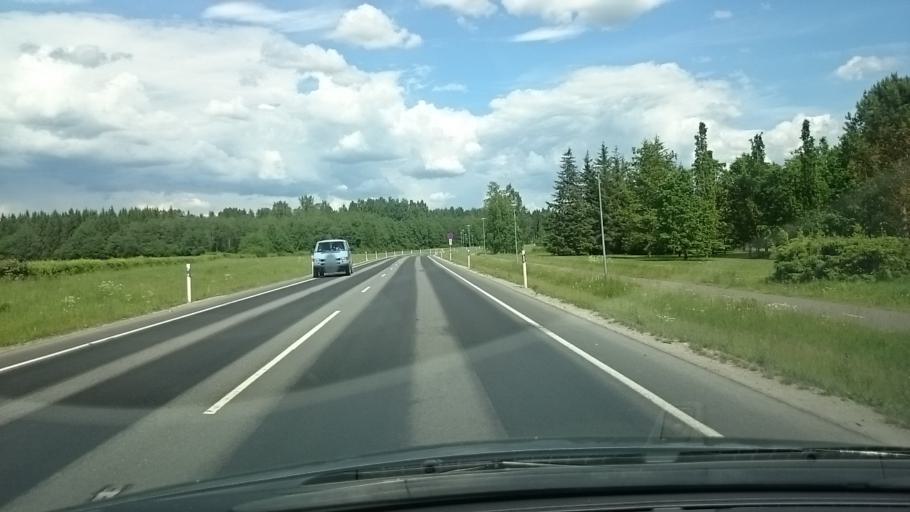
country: EE
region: Jaervamaa
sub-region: Tueri vald
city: Tueri
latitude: 58.8278
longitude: 25.4589
